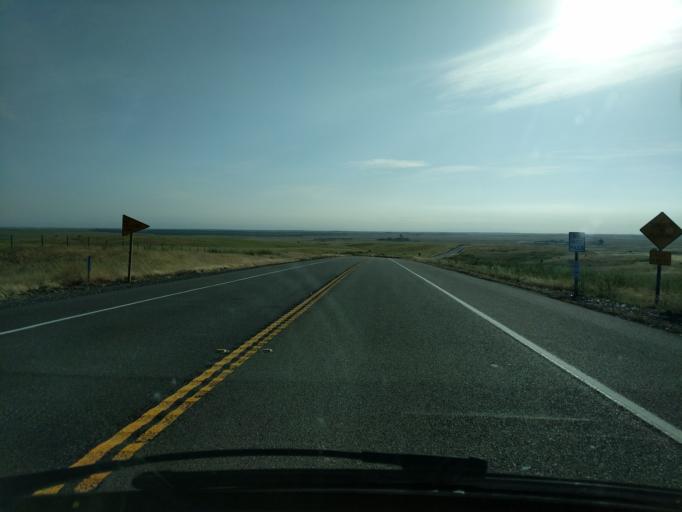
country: US
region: California
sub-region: Calaveras County
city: Copperopolis
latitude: 37.9380
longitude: -120.7808
